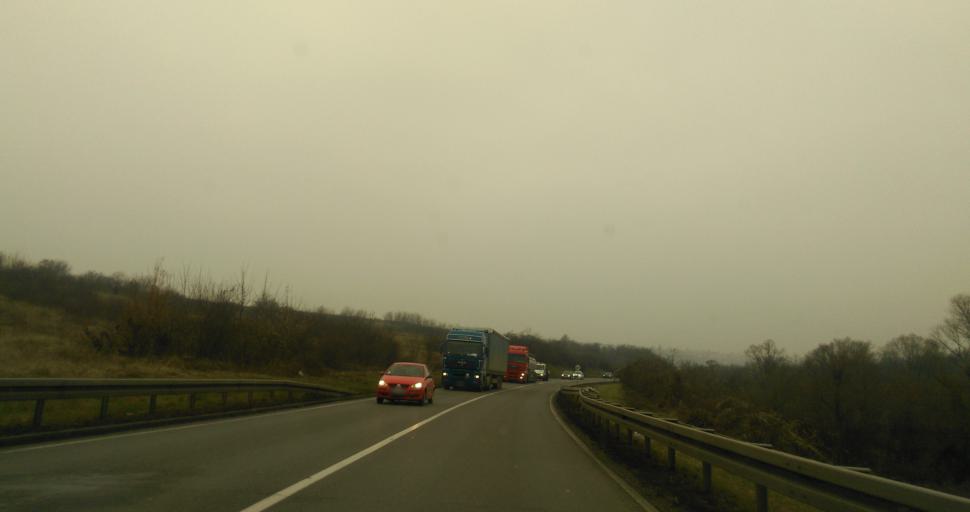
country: RS
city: Rusanj
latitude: 44.7142
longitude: 20.4829
